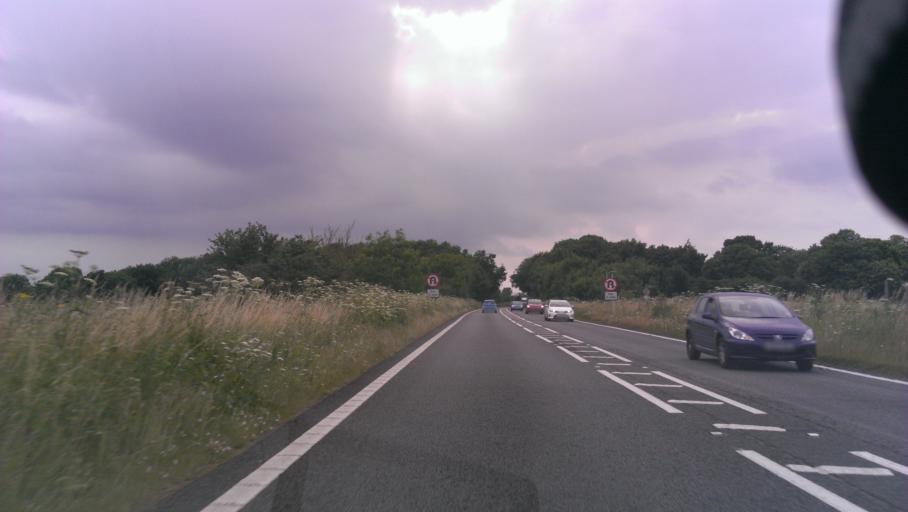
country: GB
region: England
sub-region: Kent
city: Shepherdswell
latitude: 51.1726
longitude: 1.2360
